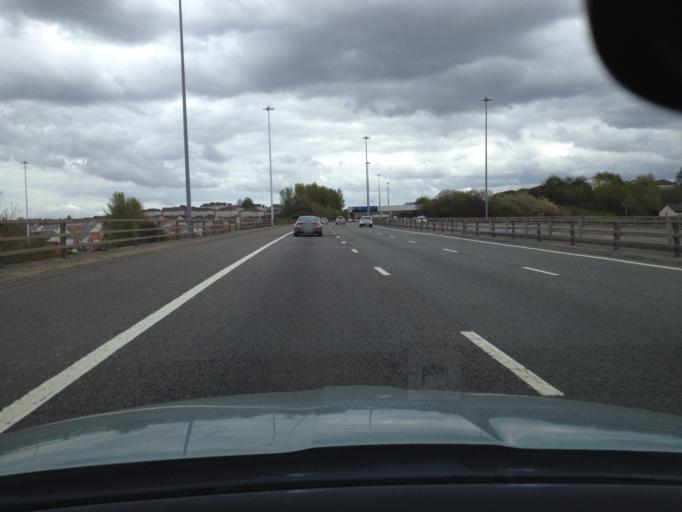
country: GB
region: Scotland
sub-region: East Dunbartonshire
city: Bishopbriggs
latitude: 55.8705
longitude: -4.2005
